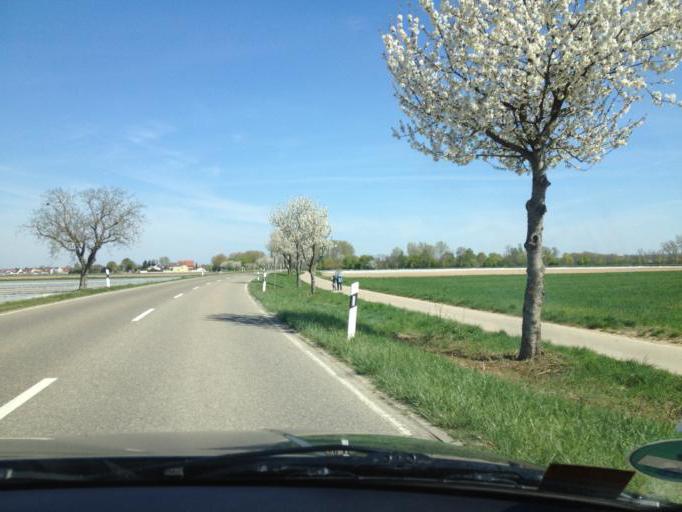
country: DE
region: Rheinland-Pfalz
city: Otterstadt
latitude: 49.3778
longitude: 8.4361
